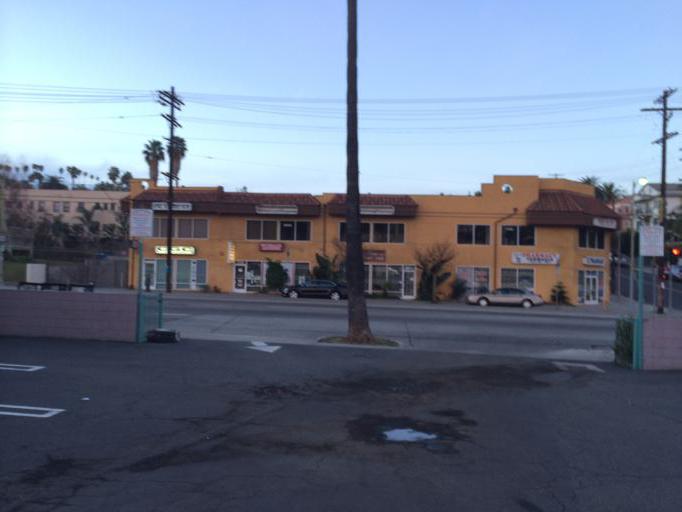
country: US
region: California
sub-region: Los Angeles County
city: Silver Lake
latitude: 34.0911
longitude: -118.2784
